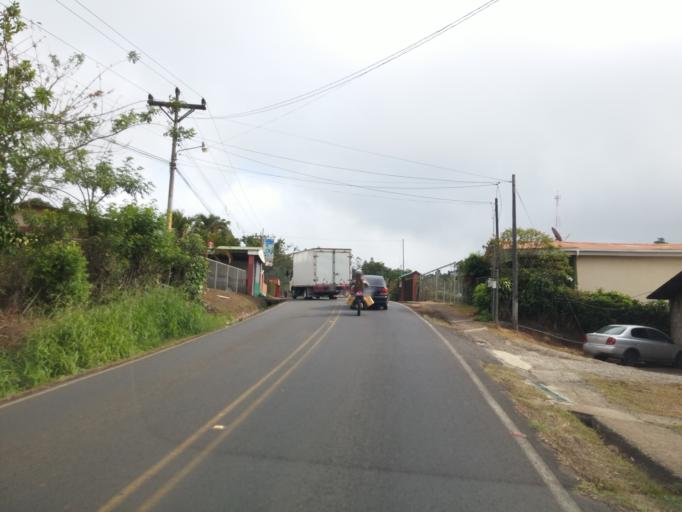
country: CR
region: Alajuela
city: San Ramon
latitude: 10.1221
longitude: -84.4734
